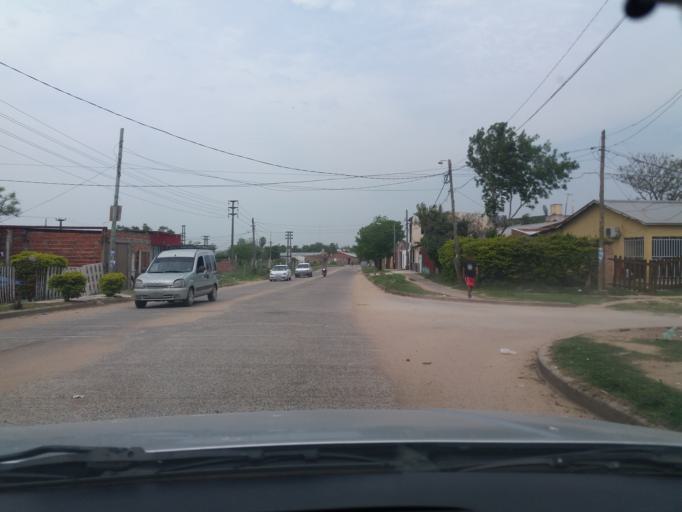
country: AR
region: Corrientes
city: Corrientes
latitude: -27.5097
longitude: -58.7981
